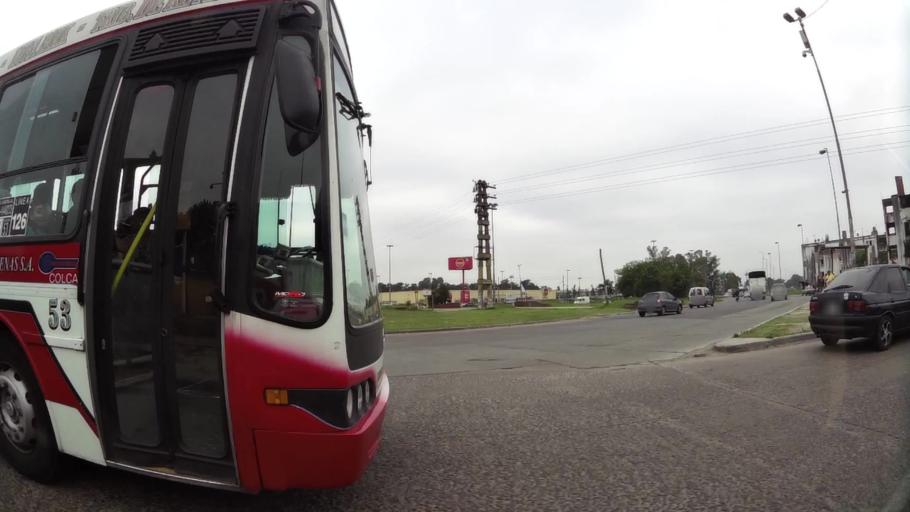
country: AR
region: Buenos Aires
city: San Justo
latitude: -34.7001
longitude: -58.5422
